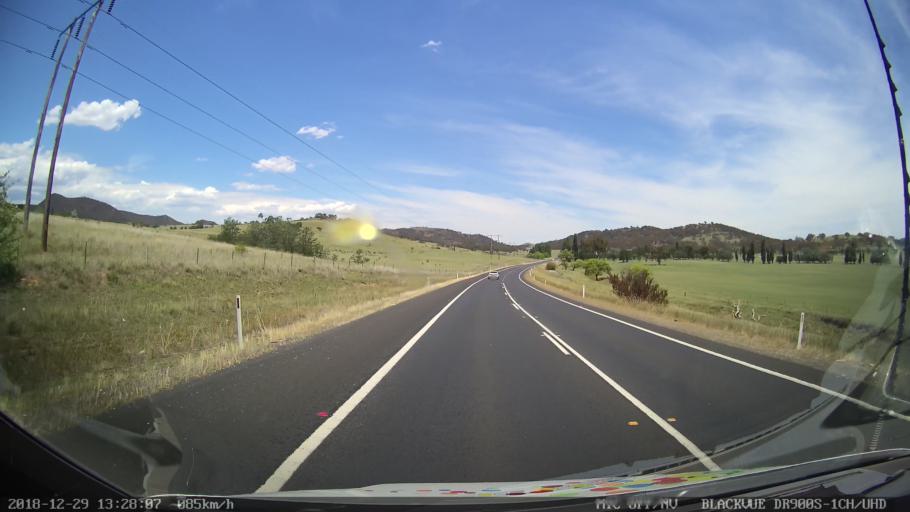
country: AU
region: New South Wales
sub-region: Cooma-Monaro
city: Cooma
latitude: -35.8711
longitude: 149.1613
